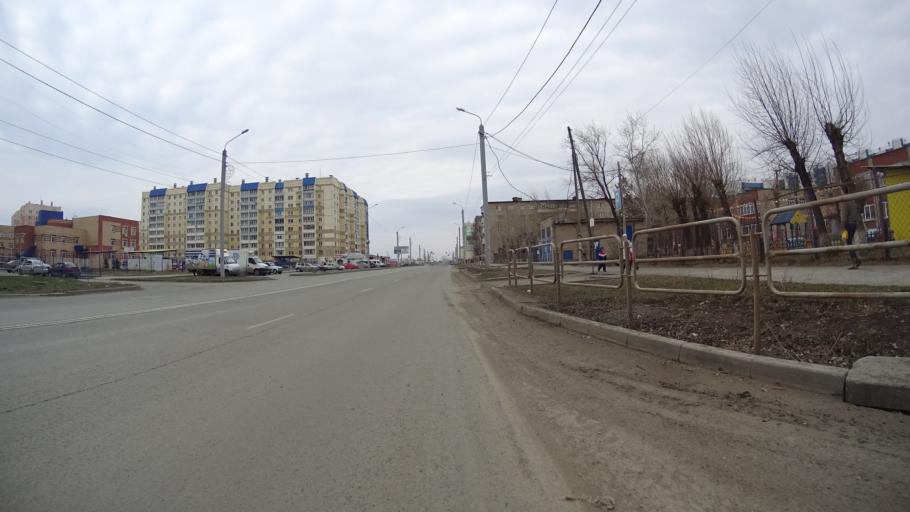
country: RU
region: Chelyabinsk
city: Zheleznodorozhnyy
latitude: 55.1693
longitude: 61.5304
